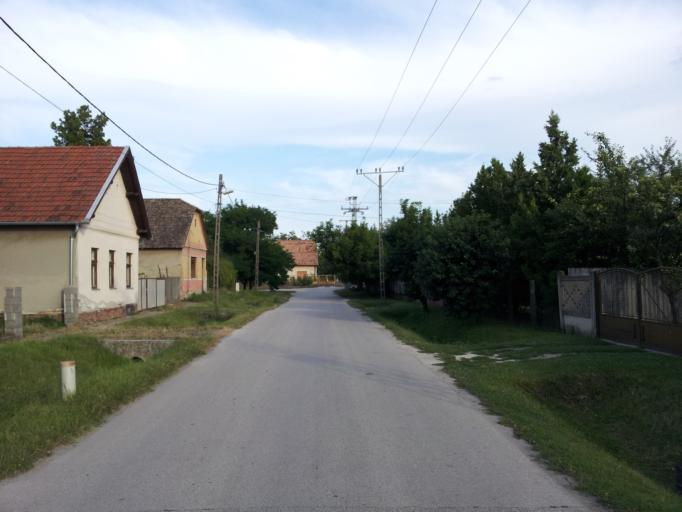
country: HU
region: Pest
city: Kiskunlachaza
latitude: 47.1928
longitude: 19.0114
